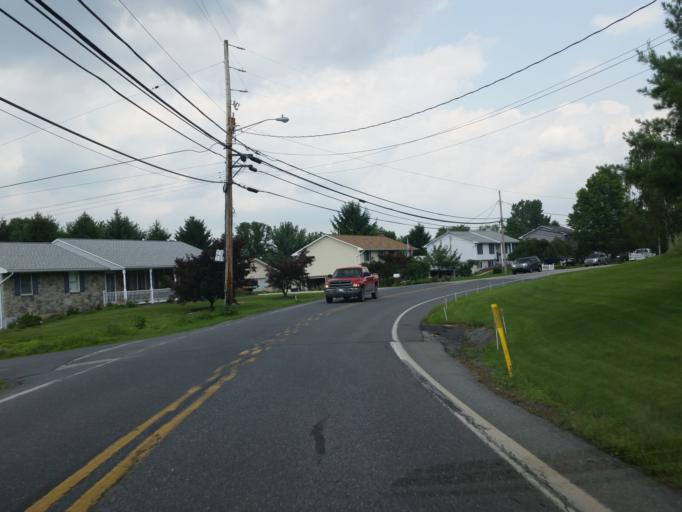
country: US
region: Pennsylvania
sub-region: Lebanon County
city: Campbelltown
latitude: 40.2695
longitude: -76.5917
